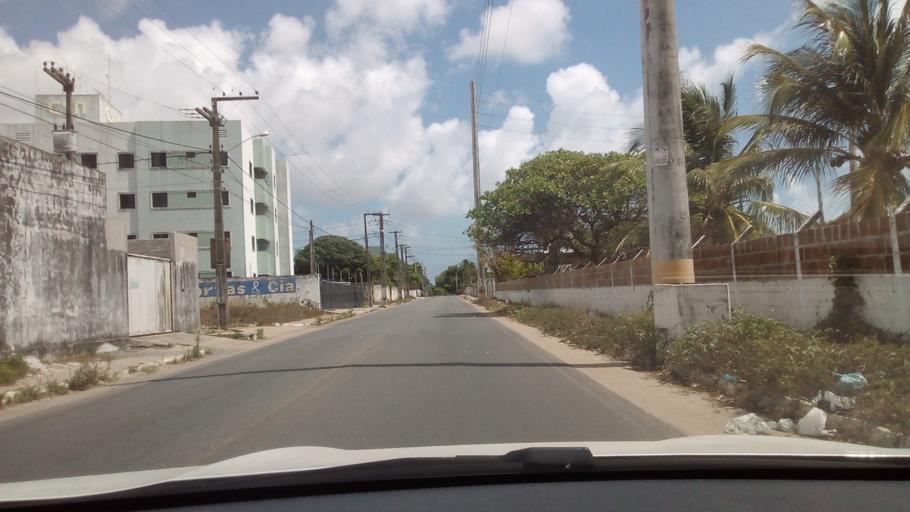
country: BR
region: Paraiba
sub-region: Conde
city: Conde
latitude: -7.2117
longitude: -34.8299
